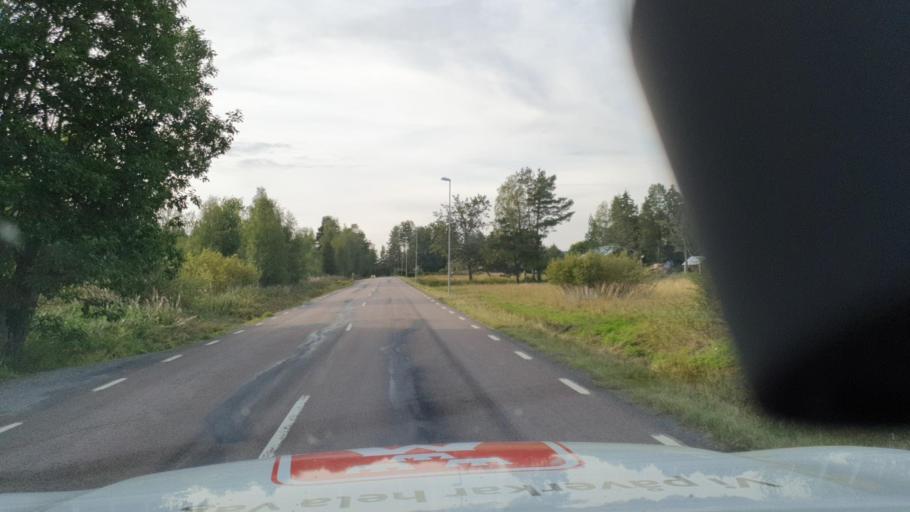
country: SE
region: Jaemtland
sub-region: Stroemsunds Kommun
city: Stroemsund
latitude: 63.8054
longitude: 15.6924
